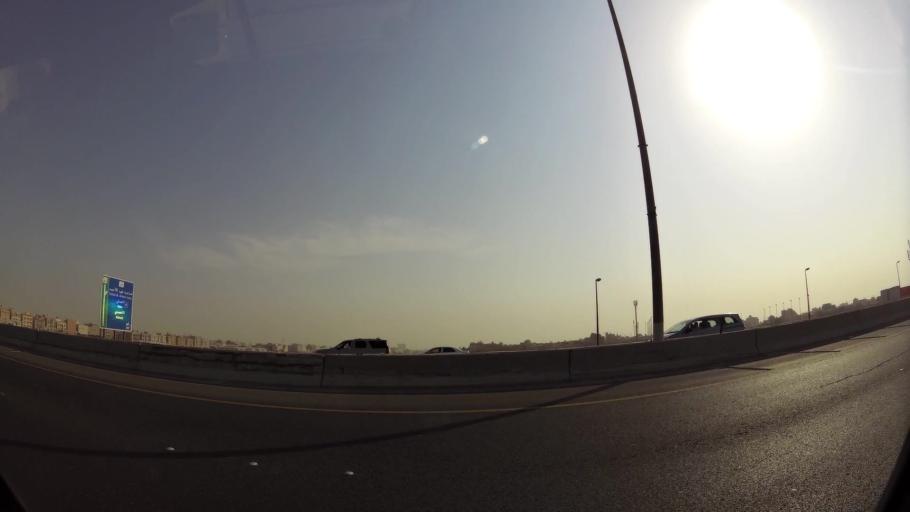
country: KW
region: Al Ahmadi
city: Ar Riqqah
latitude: 29.1185
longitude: 48.0937
